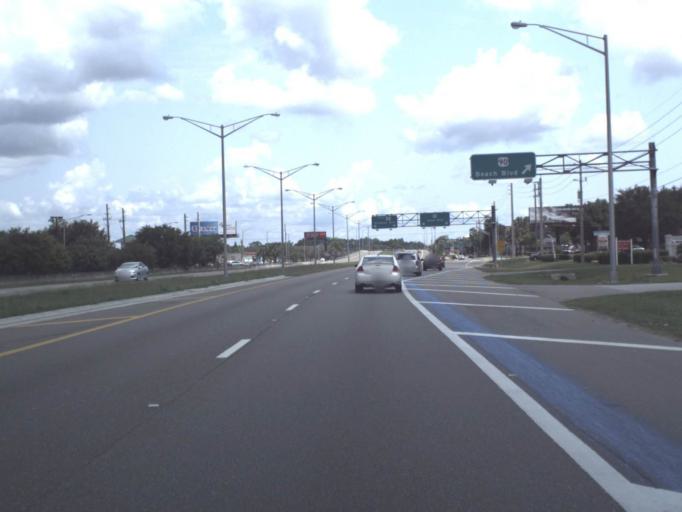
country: US
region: Florida
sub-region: Duval County
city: Jacksonville
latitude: 30.2814
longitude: -81.5590
